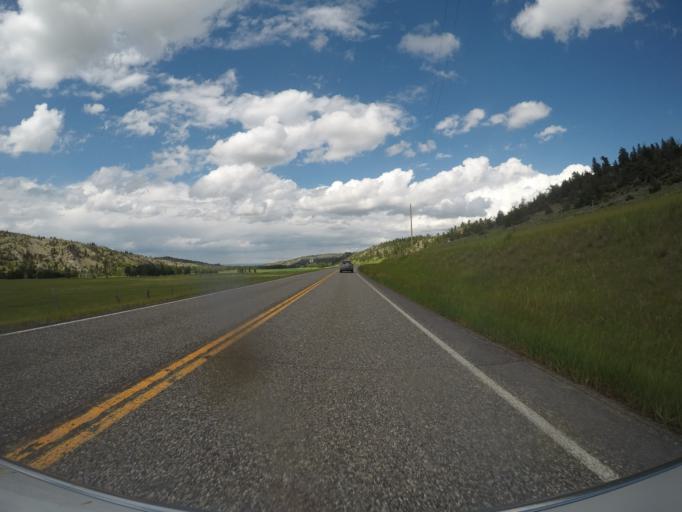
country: US
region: Montana
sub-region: Sweet Grass County
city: Big Timber
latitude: 45.7115
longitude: -110.0044
